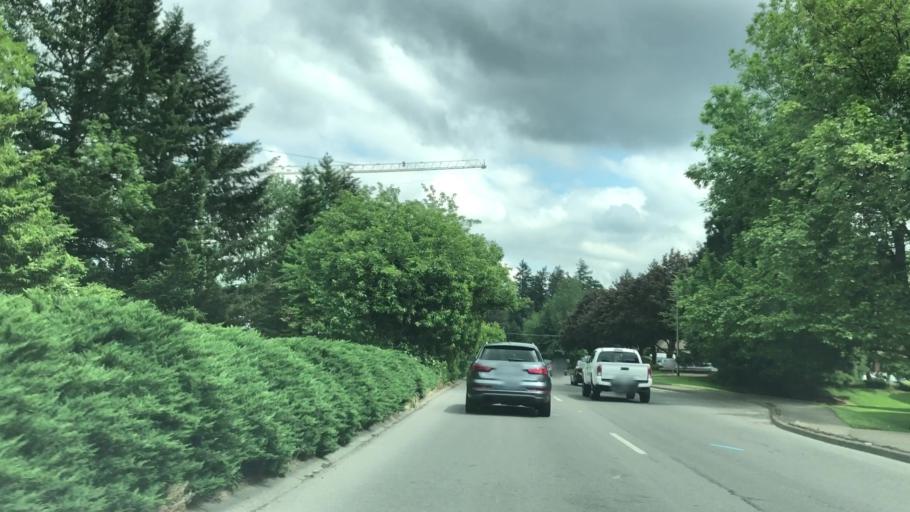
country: US
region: Oregon
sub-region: Washington County
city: Durham
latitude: 45.4166
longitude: -122.7188
